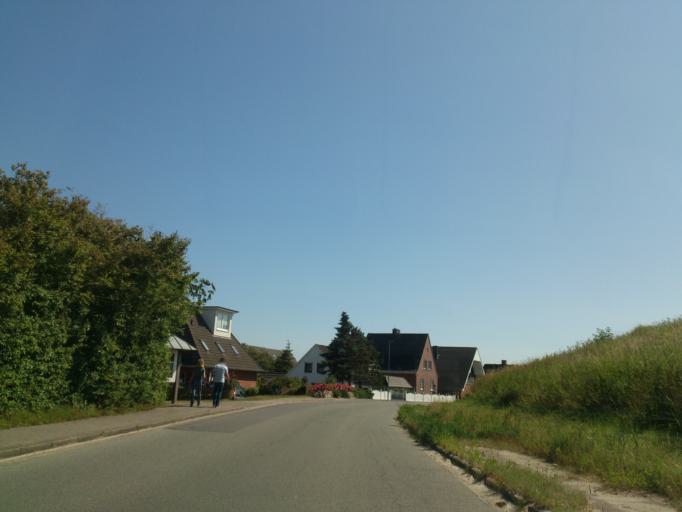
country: DE
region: Schleswig-Holstein
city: Sankt Peter-Ording
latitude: 54.3292
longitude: 8.6076
